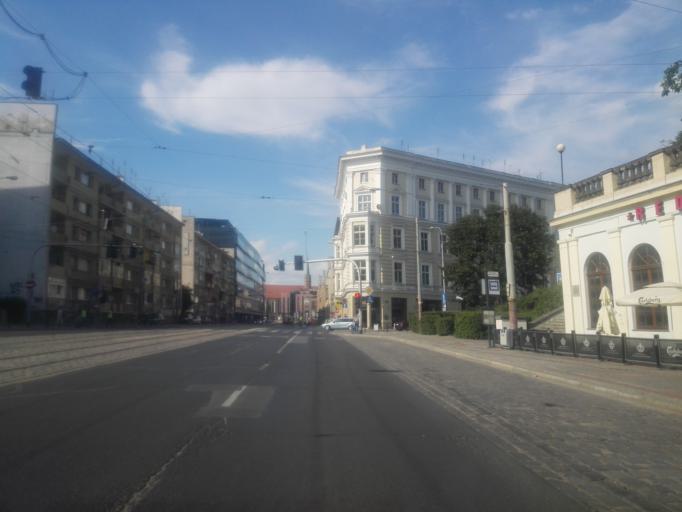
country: PL
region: Lower Silesian Voivodeship
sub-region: Powiat wroclawski
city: Wroclaw
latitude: 51.1048
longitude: 17.0378
